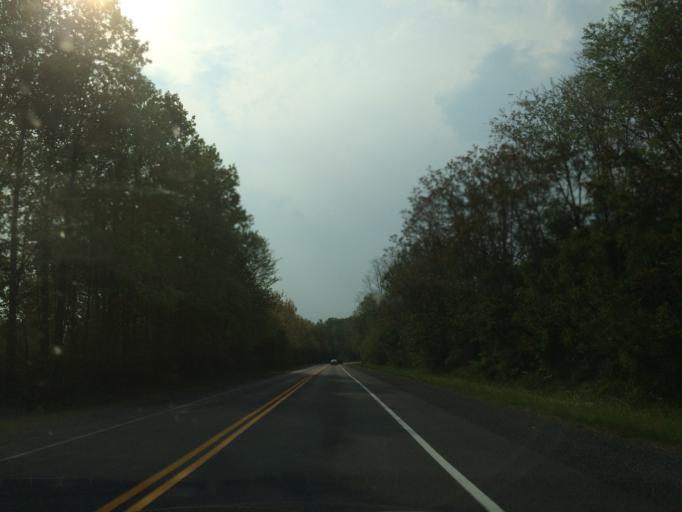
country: US
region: Maryland
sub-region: Carroll County
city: Mount Airy
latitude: 39.3518
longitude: -77.1134
